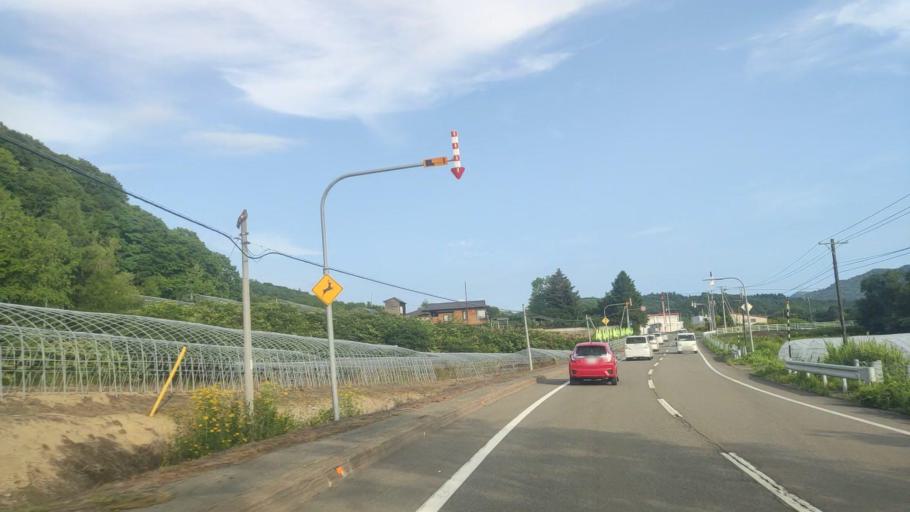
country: JP
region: Hokkaido
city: Iwamizawa
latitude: 43.0404
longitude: 141.9170
